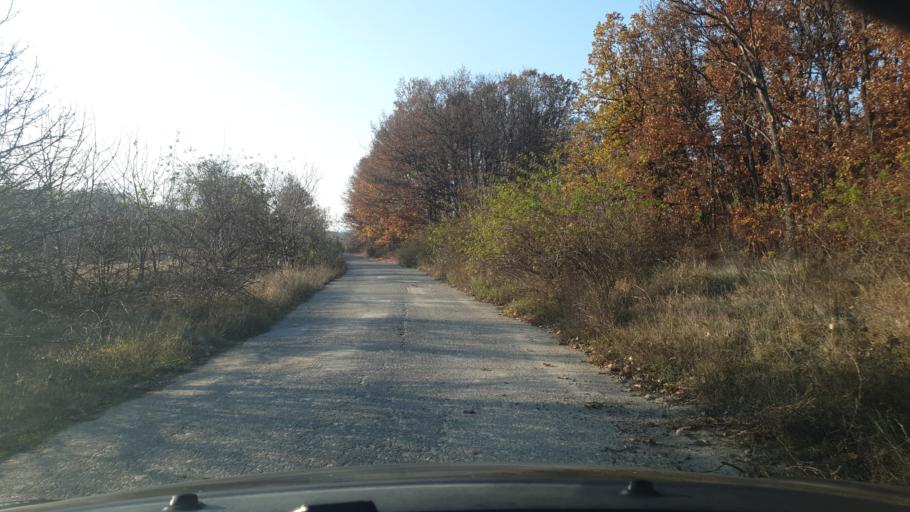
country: RS
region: Central Serbia
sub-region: Borski Okrug
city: Negotin
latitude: 44.1484
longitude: 22.3522
